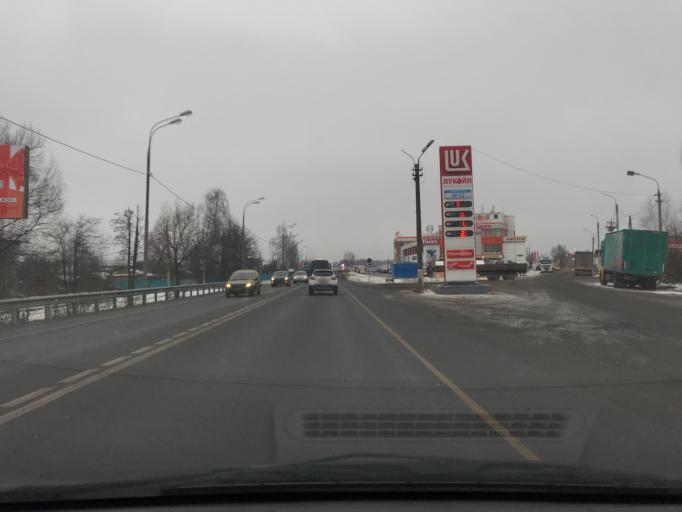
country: RU
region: Moskovskaya
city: Elektrostal'
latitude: 55.8105
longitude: 38.4268
